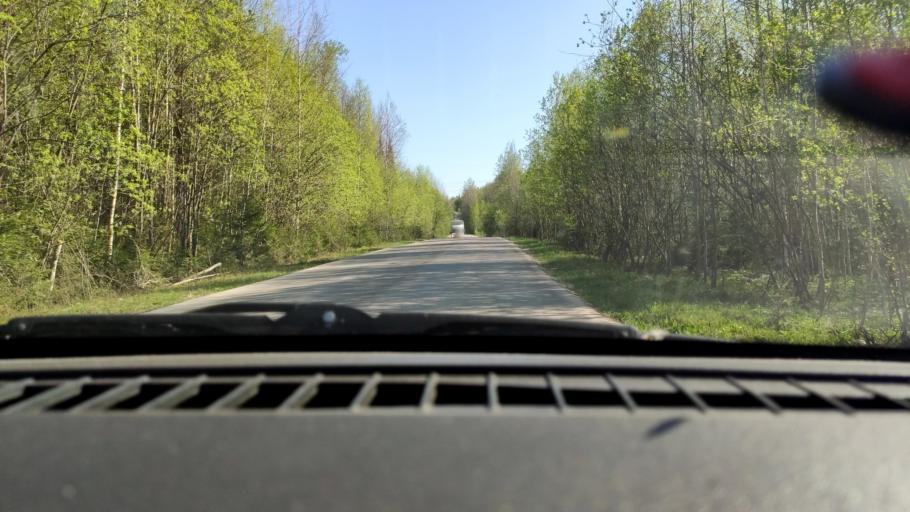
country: RU
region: Perm
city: Overyata
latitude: 58.0729
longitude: 56.0014
